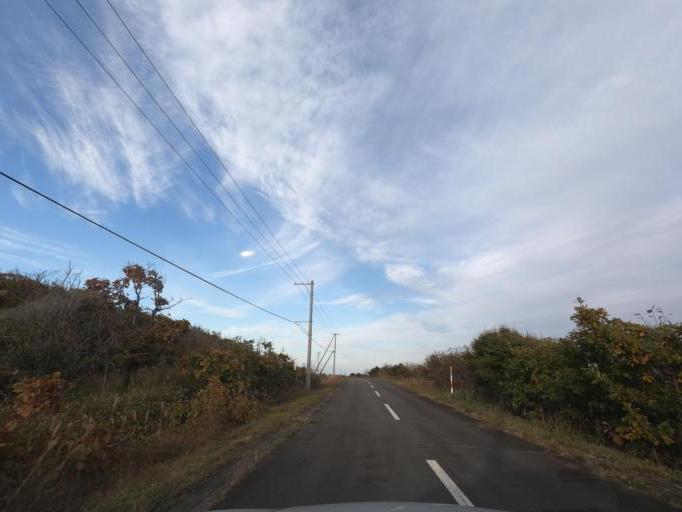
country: JP
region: Hokkaido
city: Obihiro
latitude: 42.5376
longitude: 143.4878
